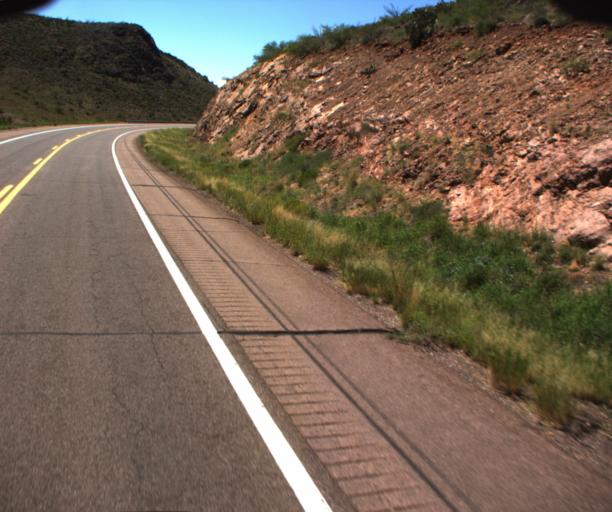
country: US
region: Arizona
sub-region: Greenlee County
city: Clifton
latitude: 32.8472
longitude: -109.3909
